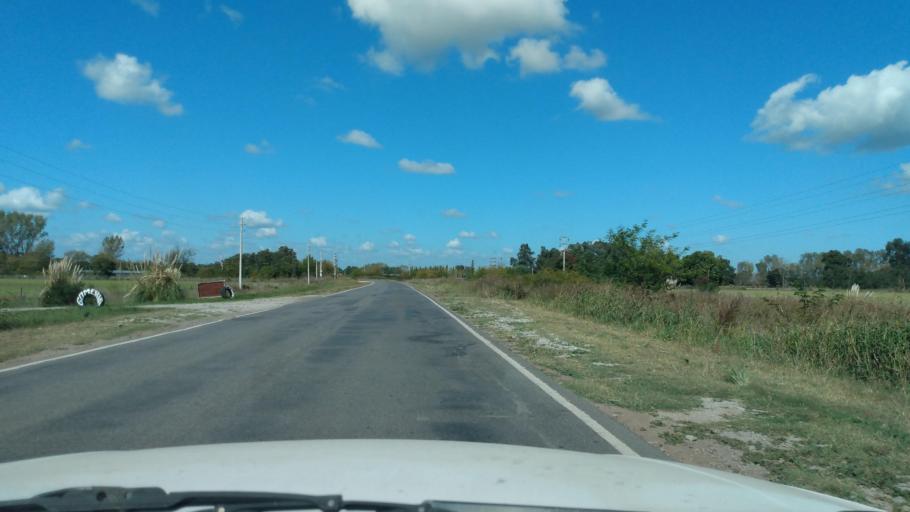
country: AR
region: Buenos Aires
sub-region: Partido de Mercedes
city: Mercedes
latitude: -34.6998
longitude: -59.4033
